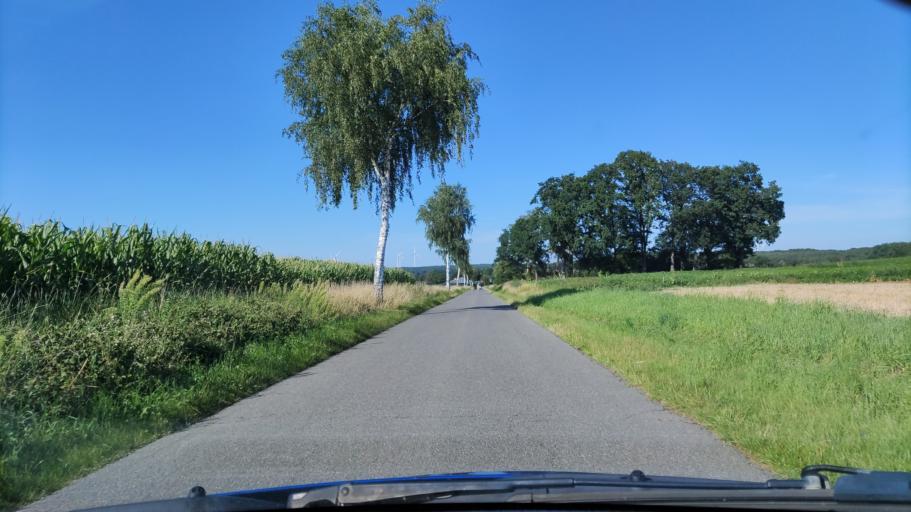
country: DE
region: Lower Saxony
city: Boitze
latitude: 53.1565
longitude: 10.7546
